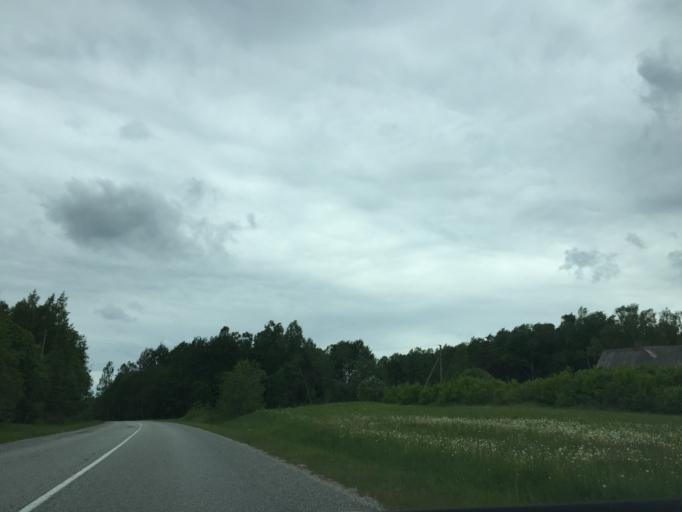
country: LV
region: Aglona
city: Aglona
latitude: 56.1384
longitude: 27.0876
